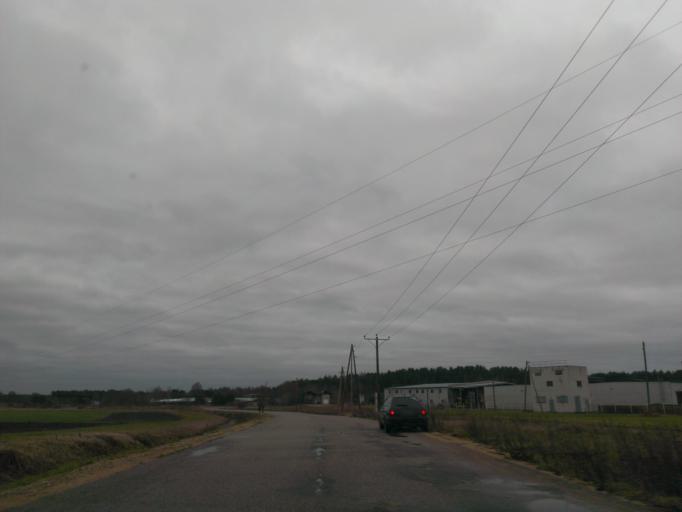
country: LV
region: Adazi
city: Adazi
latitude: 57.0651
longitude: 24.3328
